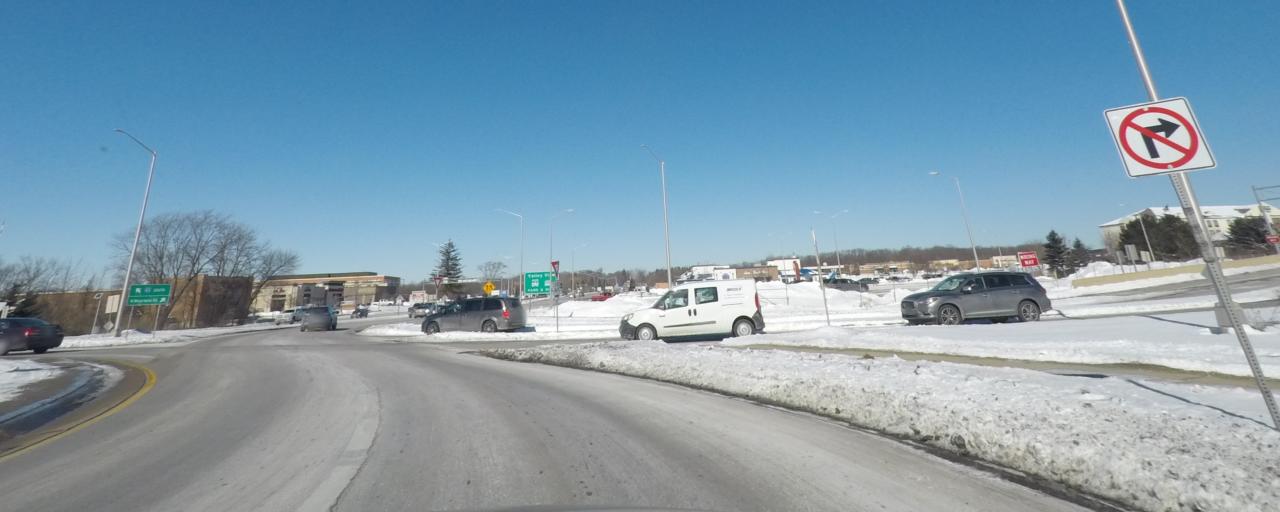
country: US
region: Wisconsin
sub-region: Waukesha County
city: New Berlin
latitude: 42.9535
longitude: -88.1084
